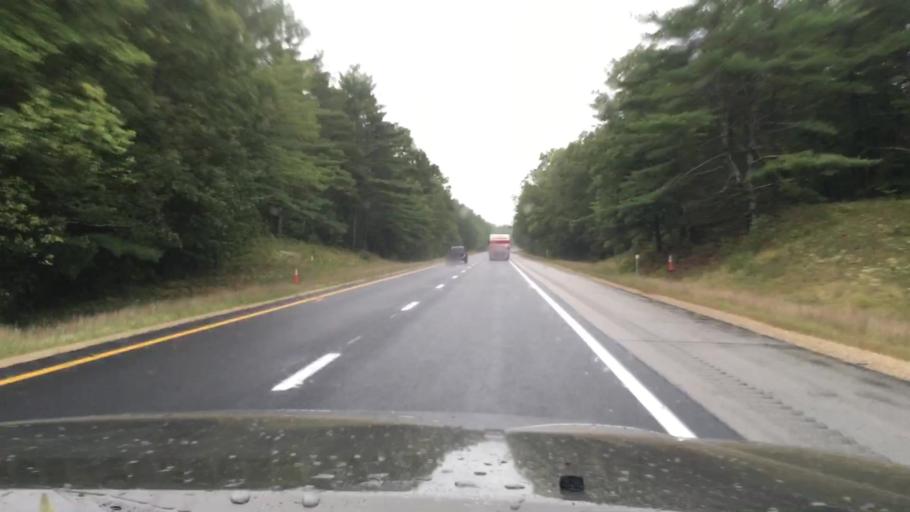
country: US
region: New Hampshire
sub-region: Merrimack County
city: Boscawen
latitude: 43.3604
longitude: -71.6124
